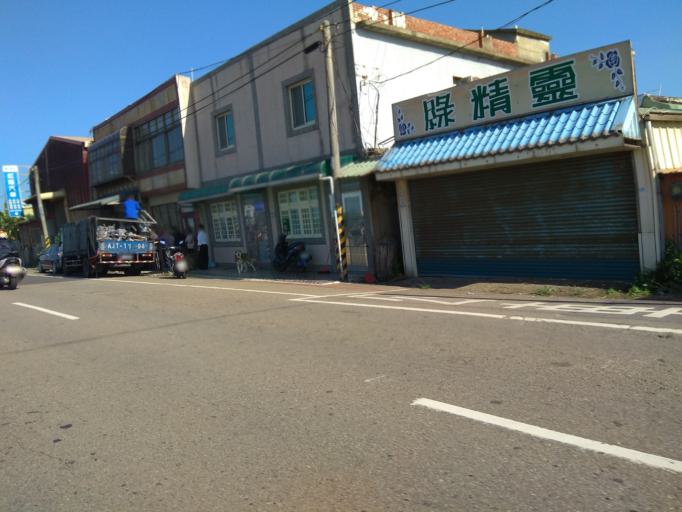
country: TW
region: Taiwan
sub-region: Hsinchu
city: Zhubei
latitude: 25.0128
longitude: 121.0497
